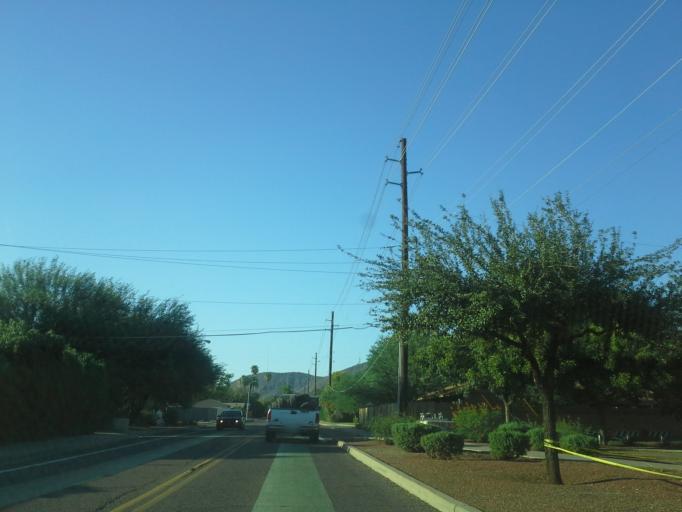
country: US
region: Arizona
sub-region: Maricopa County
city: Glendale
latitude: 33.5636
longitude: -112.0913
